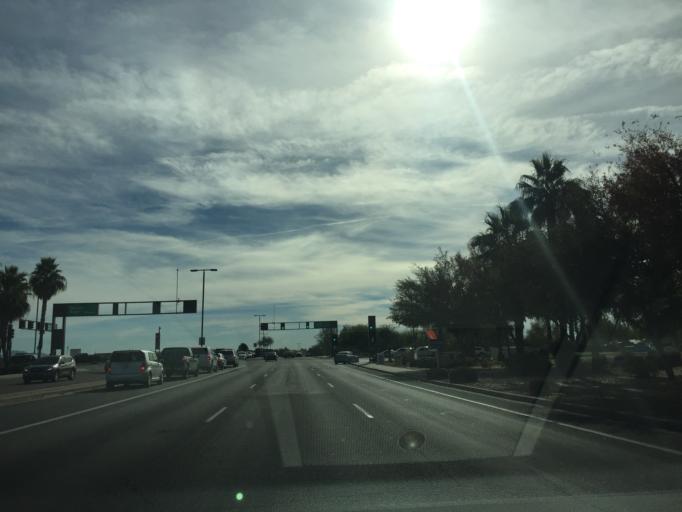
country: US
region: Arizona
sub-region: Maricopa County
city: Gilbert
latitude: 33.3362
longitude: -111.7901
